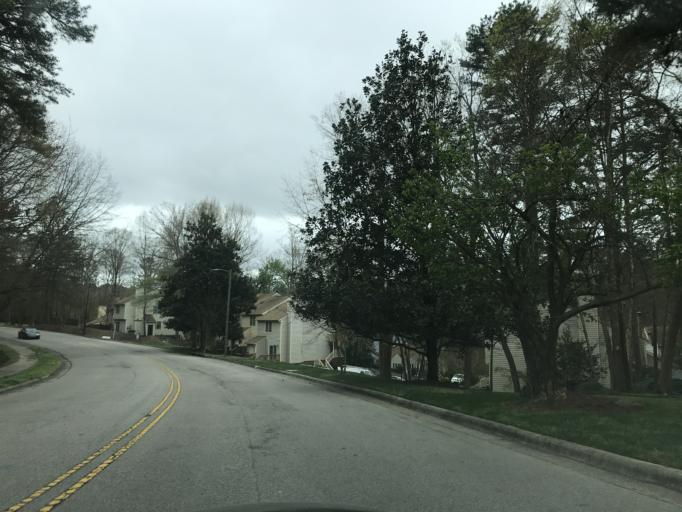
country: US
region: North Carolina
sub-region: Wake County
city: West Raleigh
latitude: 35.8708
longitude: -78.6487
